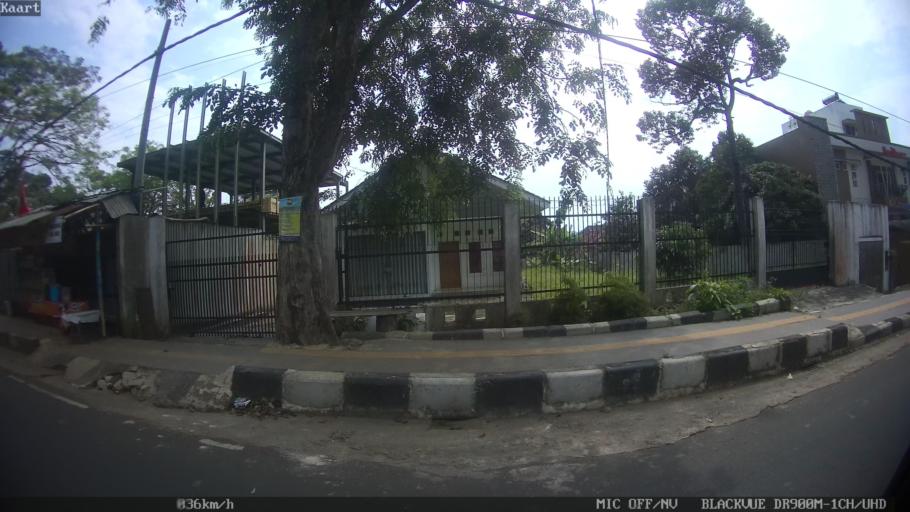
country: ID
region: Lampung
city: Bandarlampung
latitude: -5.4333
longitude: 105.2497
